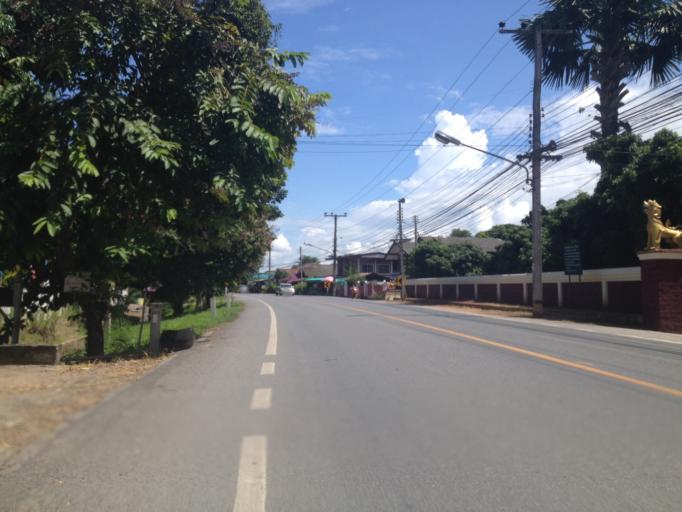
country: TH
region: Chiang Mai
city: San Pa Tong
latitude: 18.6146
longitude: 98.9550
